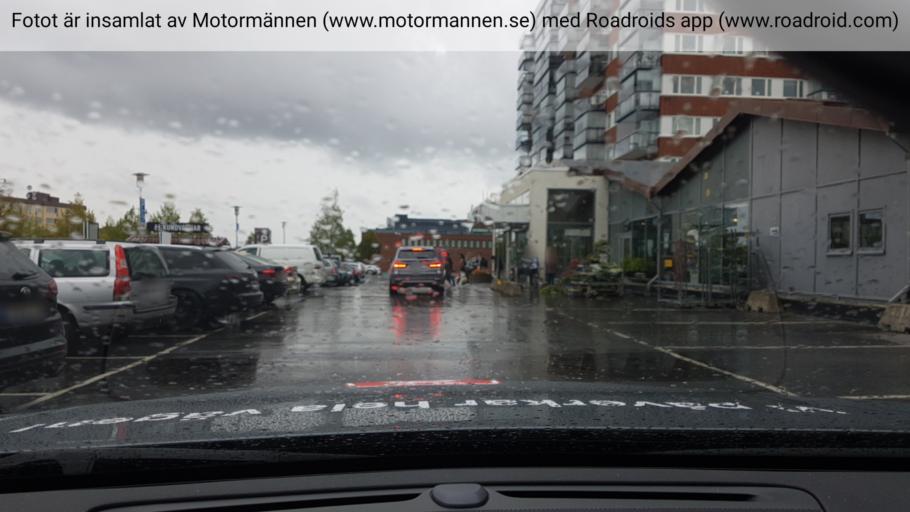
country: SE
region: Stockholm
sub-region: Haninge Kommun
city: Handen
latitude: 59.1688
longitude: 18.1394
